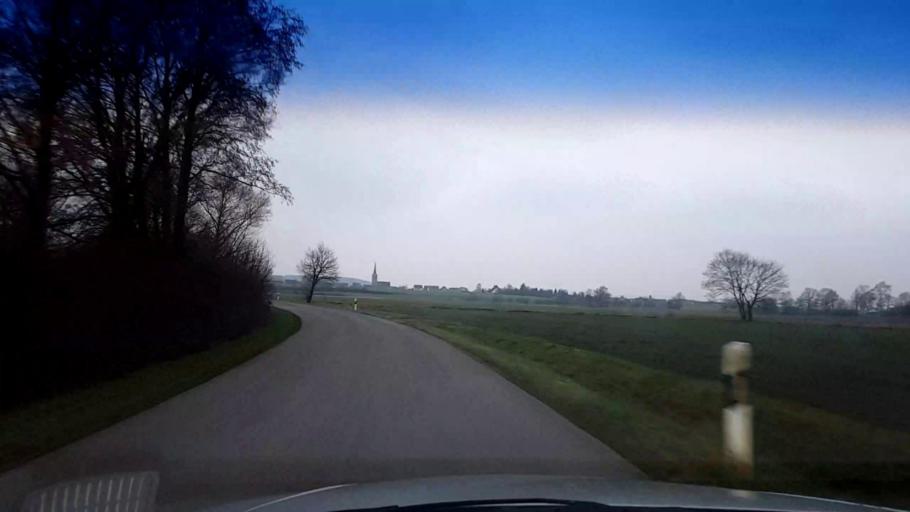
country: DE
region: Bavaria
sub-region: Upper Franconia
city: Rattelsdorf
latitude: 50.0197
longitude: 10.9084
